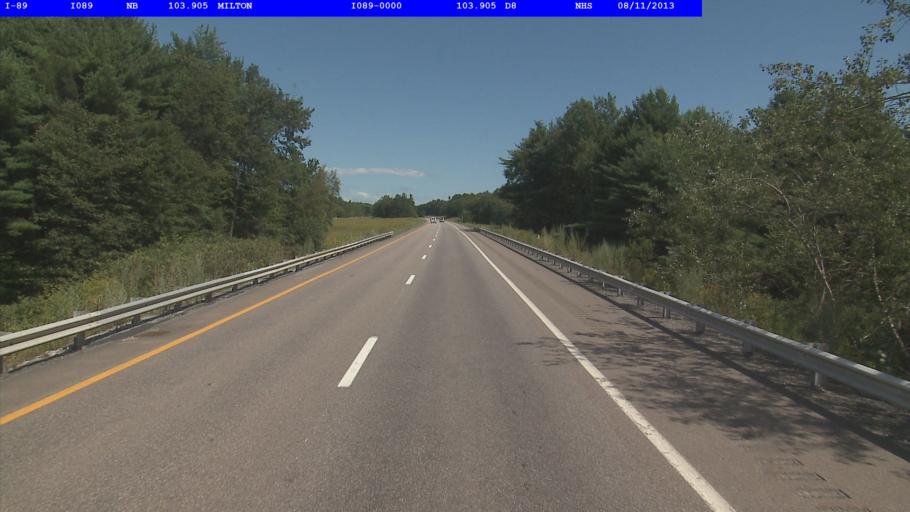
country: US
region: Vermont
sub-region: Chittenden County
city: Milton
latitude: 44.6692
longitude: -73.1336
